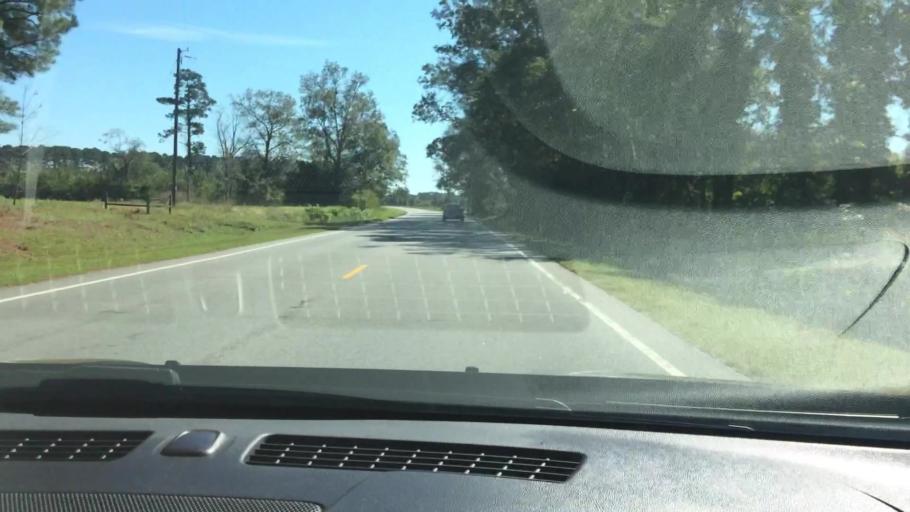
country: US
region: North Carolina
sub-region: Pitt County
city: Grifton
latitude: 35.3540
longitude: -77.3368
